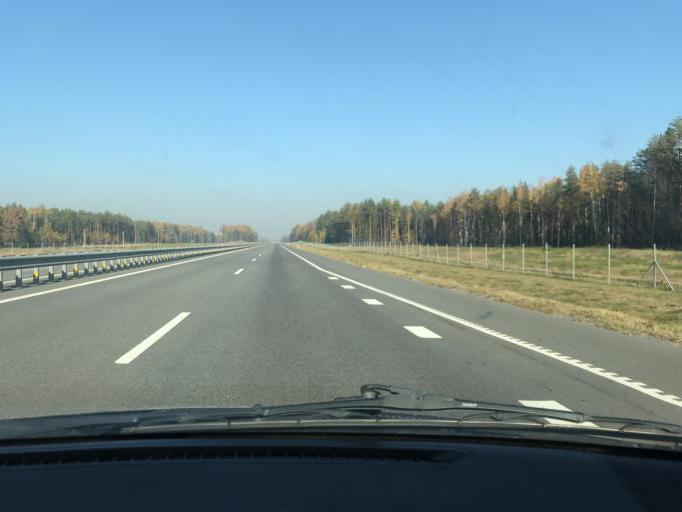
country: BY
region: Minsk
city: Slutsk
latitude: 53.2339
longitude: 27.5505
